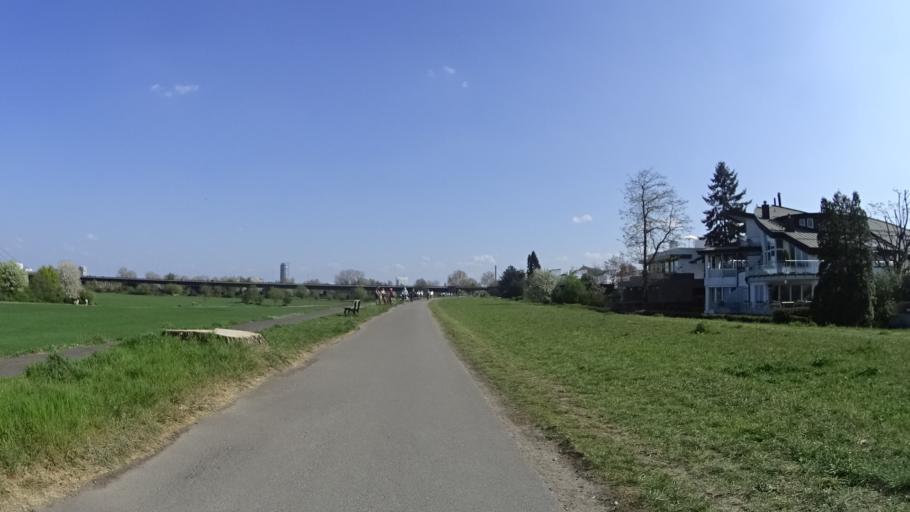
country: DE
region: North Rhine-Westphalia
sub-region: Regierungsbezirk Dusseldorf
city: Dusseldorf
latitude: 51.2454
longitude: 6.7478
